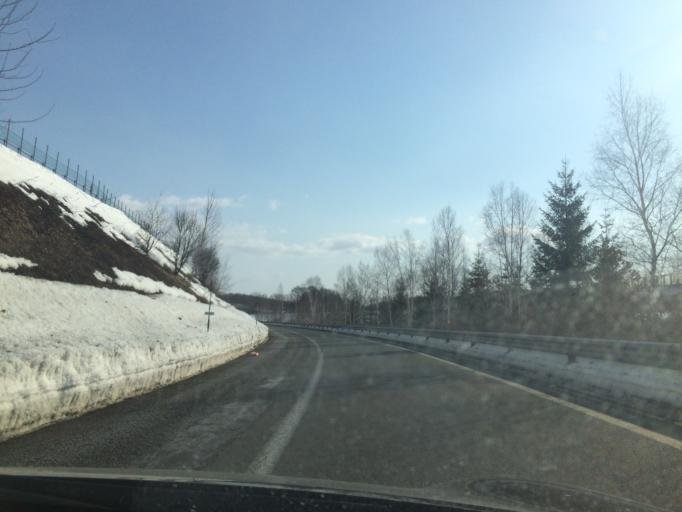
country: JP
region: Hokkaido
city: Chitose
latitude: 42.8460
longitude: 141.5840
